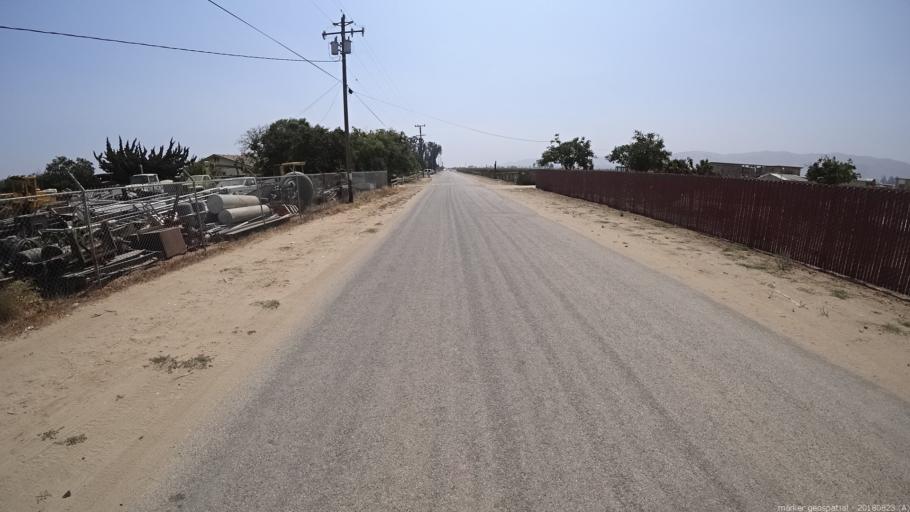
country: US
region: California
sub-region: Monterey County
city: Greenfield
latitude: 36.3282
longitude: -121.2605
